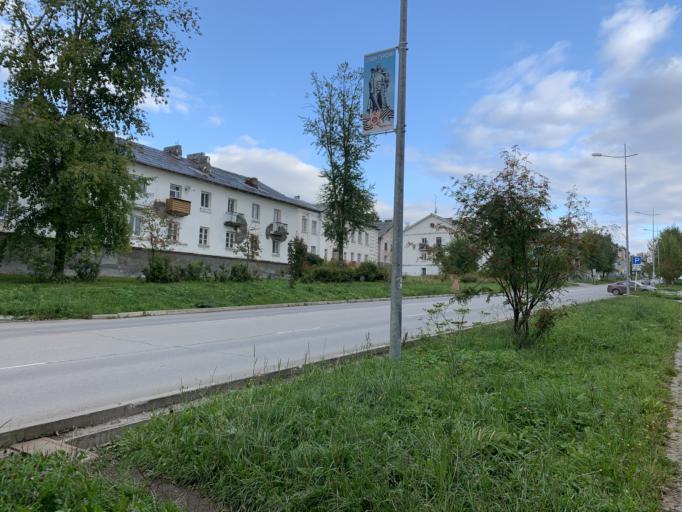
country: RU
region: Perm
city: Gubakha
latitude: 58.8449
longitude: 57.5487
